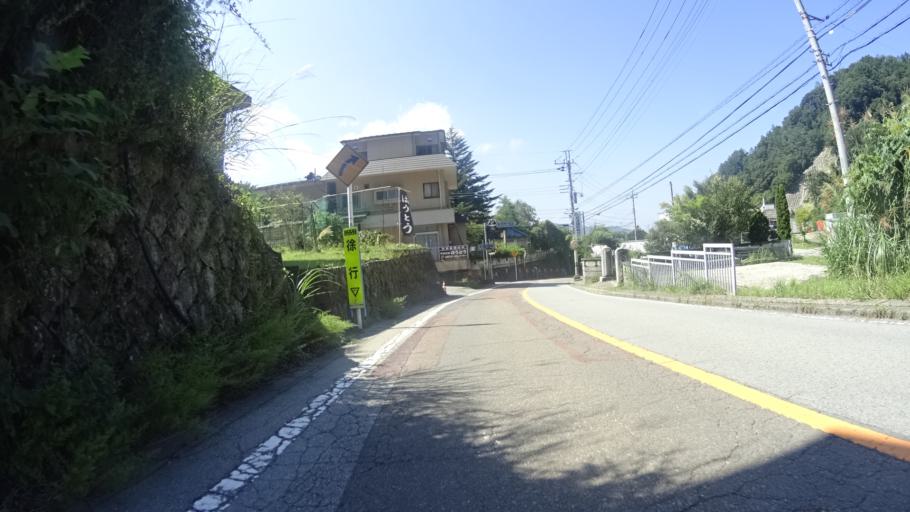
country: JP
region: Yamanashi
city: Enzan
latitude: 35.7390
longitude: 138.8021
